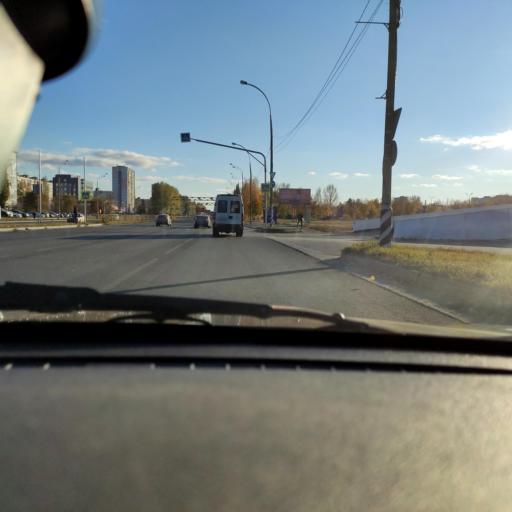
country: RU
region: Samara
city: Tol'yatti
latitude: 53.5176
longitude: 49.2787
